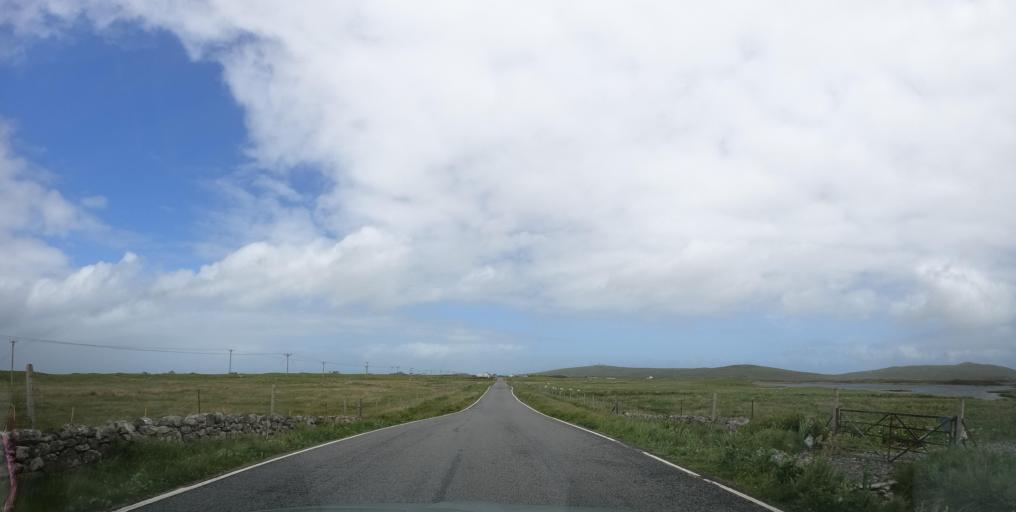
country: GB
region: Scotland
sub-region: Eilean Siar
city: Isle of South Uist
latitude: 57.3163
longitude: -7.3695
